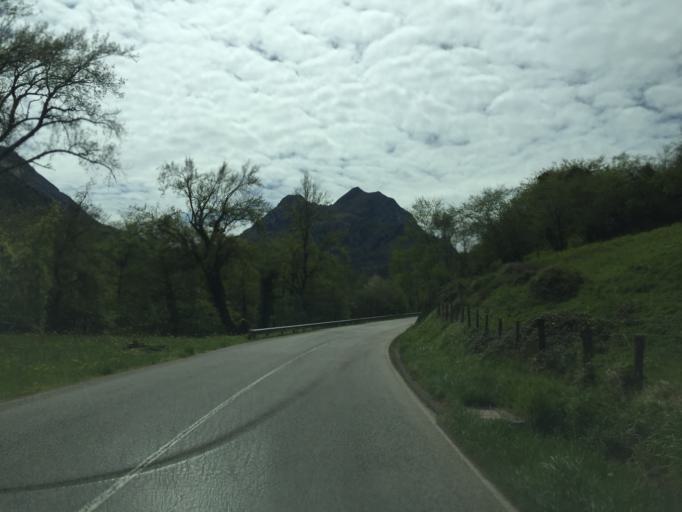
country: ES
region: Asturias
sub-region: Province of Asturias
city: Proaza
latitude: 43.2615
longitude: -6.0073
